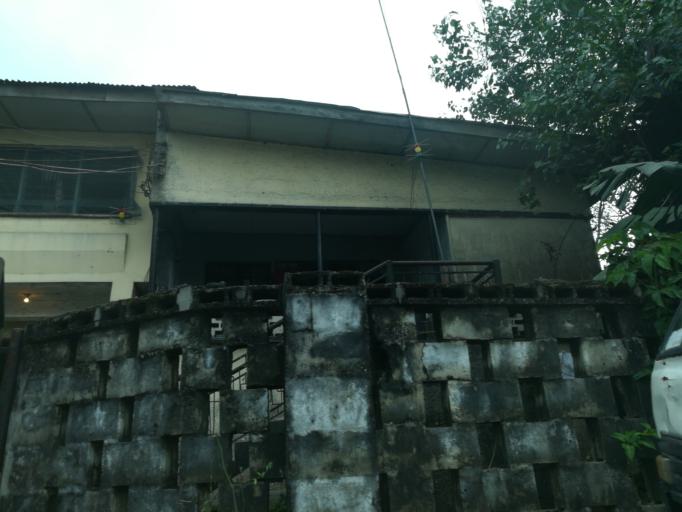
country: NG
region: Rivers
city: Port Harcourt
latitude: 4.8394
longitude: 7.0324
